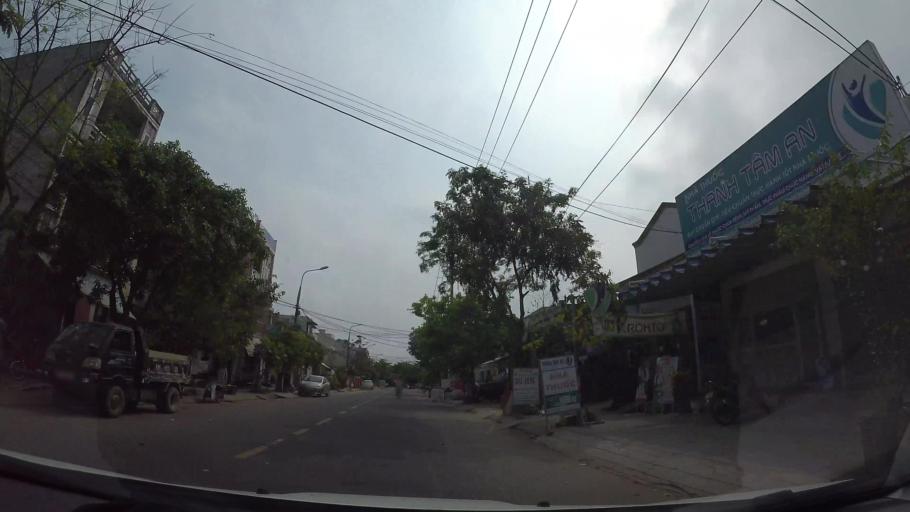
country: VN
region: Da Nang
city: Son Tra
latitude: 16.0932
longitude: 108.2460
